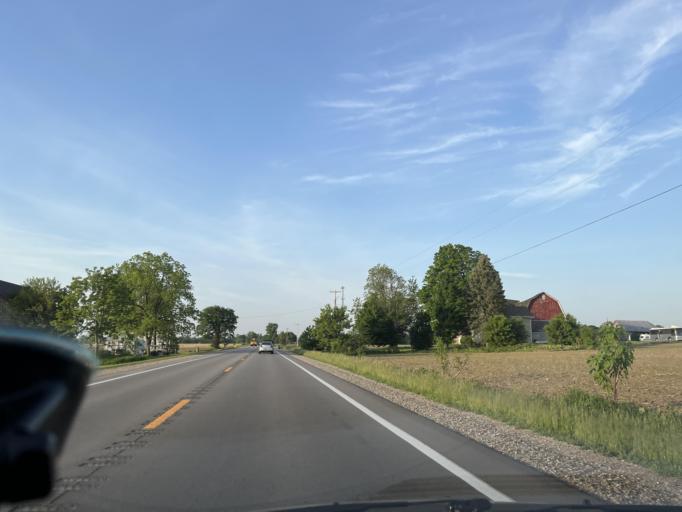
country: US
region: Michigan
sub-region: Kent County
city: Caledonia
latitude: 42.7647
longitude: -85.5064
